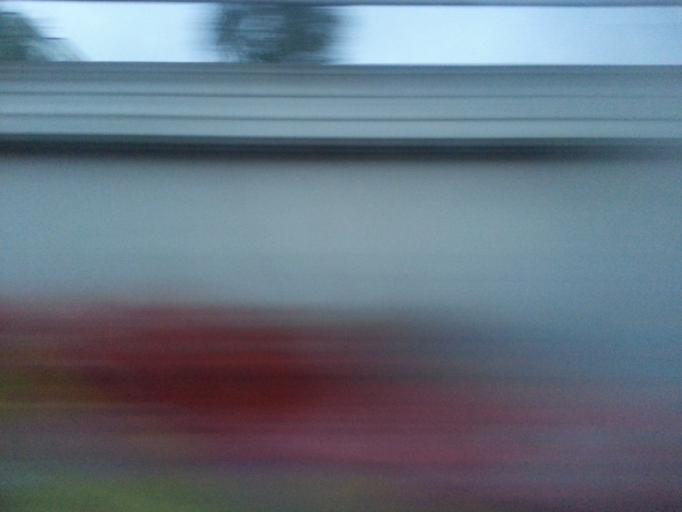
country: NO
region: Oslo
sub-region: Oslo
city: Oslo
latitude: 59.9061
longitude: 10.7944
